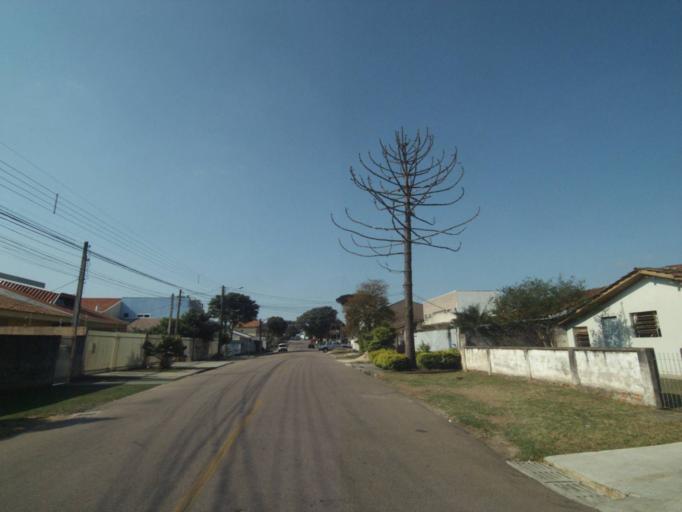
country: BR
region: Parana
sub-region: Curitiba
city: Curitiba
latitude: -25.4888
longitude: -49.3278
